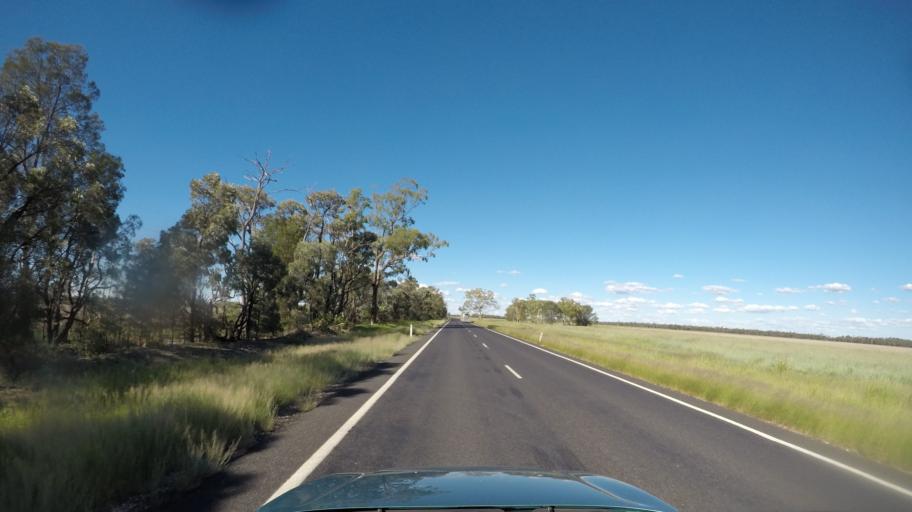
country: AU
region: Queensland
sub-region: Goondiwindi
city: Goondiwindi
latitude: -28.1415
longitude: 150.6907
